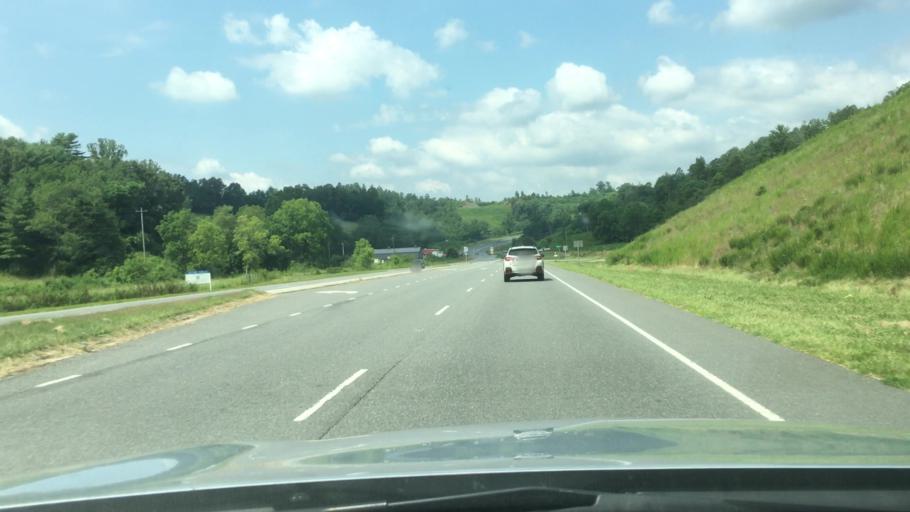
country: US
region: North Carolina
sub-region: Madison County
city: Mars Hill
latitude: 35.8430
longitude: -82.5027
